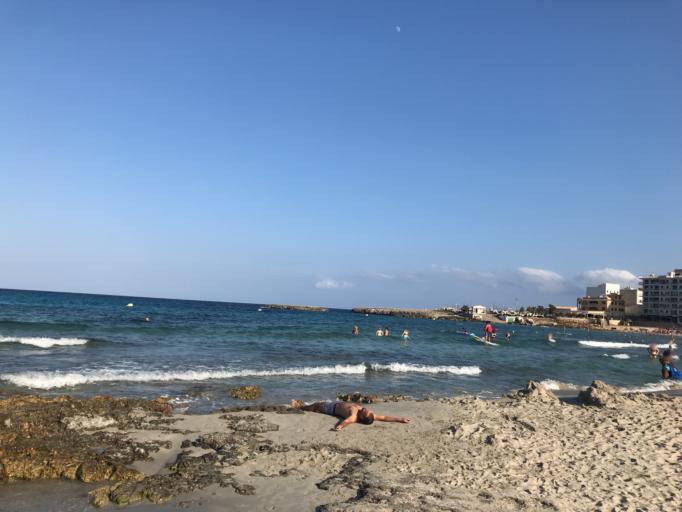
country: ES
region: Balearic Islands
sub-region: Illes Balears
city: Son Servera
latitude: 39.5669
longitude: 3.3731
